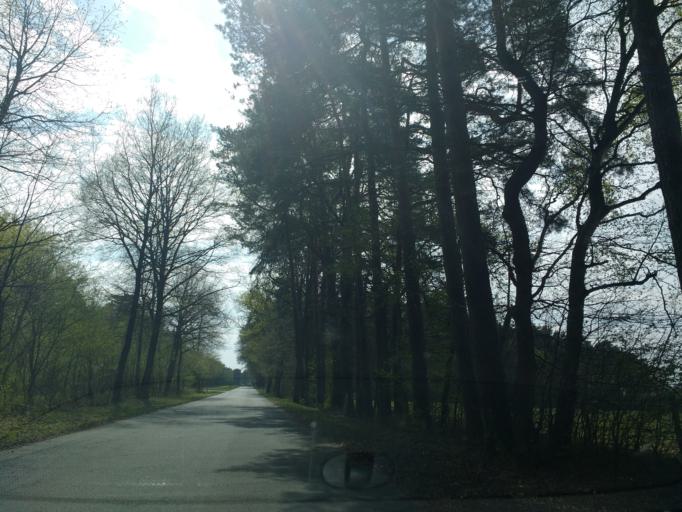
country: DE
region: North Rhine-Westphalia
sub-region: Regierungsbezirk Detmold
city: Hovelhof
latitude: 51.7919
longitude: 8.7207
